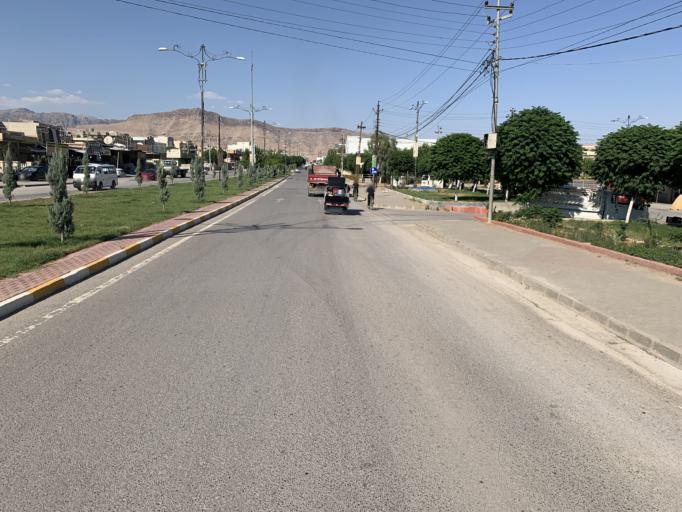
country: IQ
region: As Sulaymaniyah
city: Raniye
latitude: 36.2326
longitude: 44.7880
